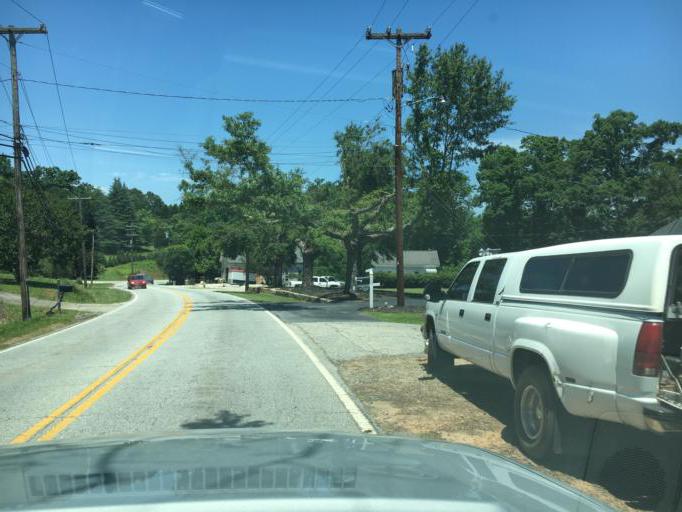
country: US
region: South Carolina
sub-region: Greenville County
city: Greer
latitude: 34.9576
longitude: -82.2083
